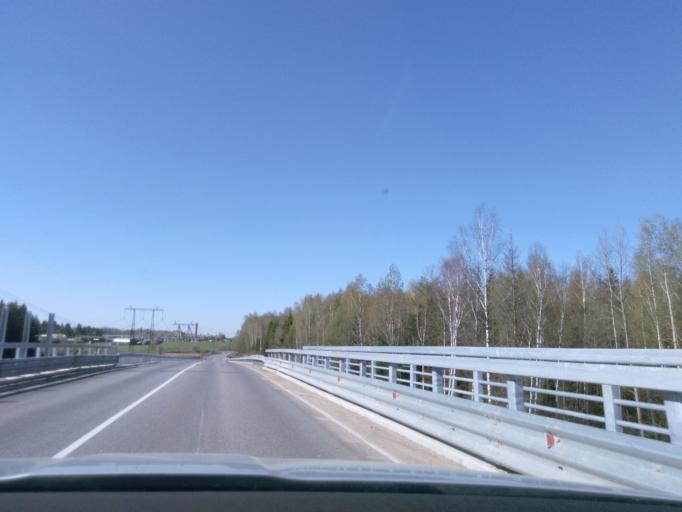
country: RU
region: Moskovskaya
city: Mendeleyevo
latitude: 56.0631
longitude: 37.2359
